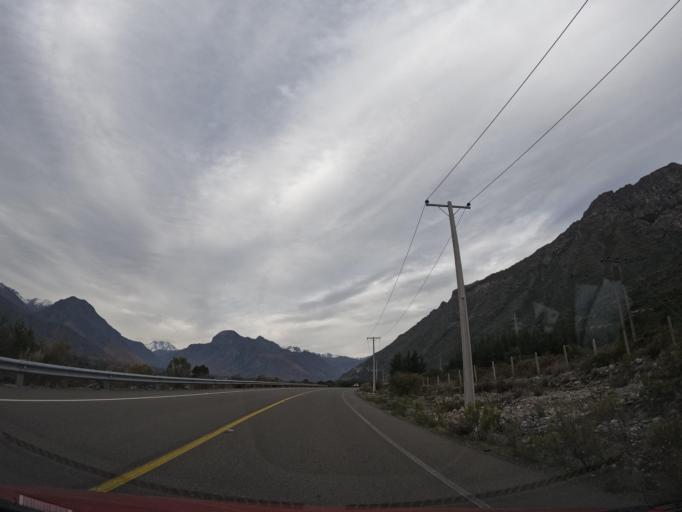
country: CL
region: Maule
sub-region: Provincia de Linares
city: Colbun
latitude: -35.7075
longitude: -71.1001
